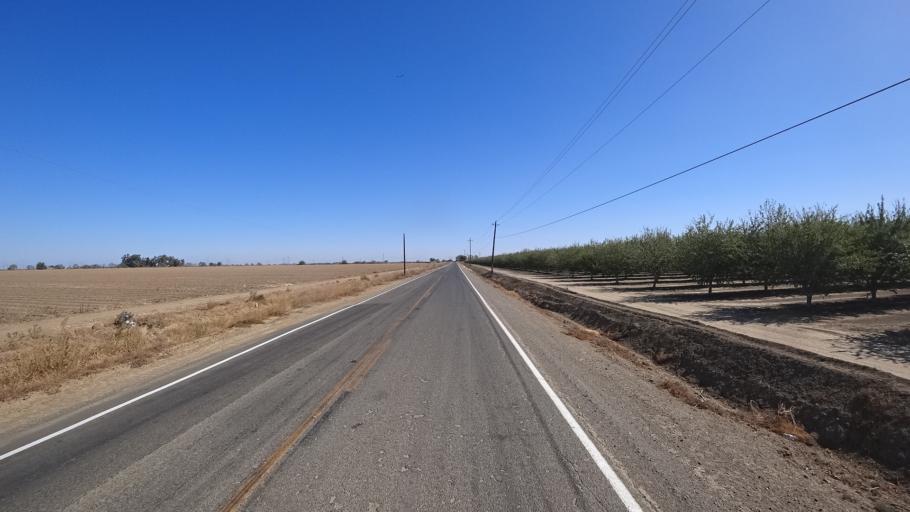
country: US
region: California
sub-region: Yolo County
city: Winters
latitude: 38.5619
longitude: -121.9430
